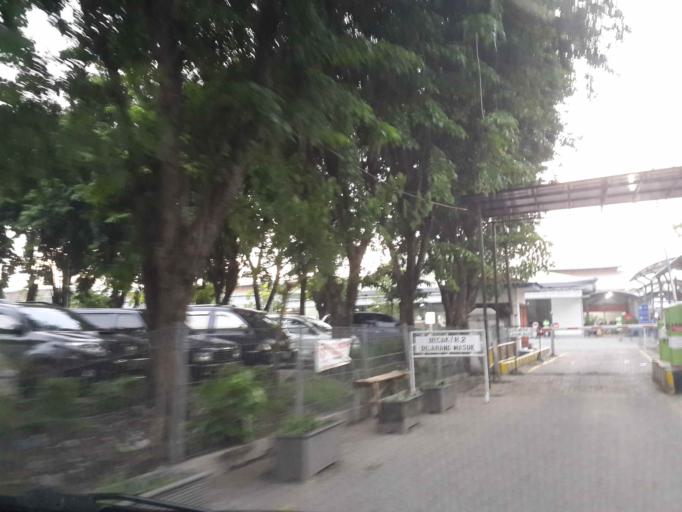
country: ID
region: East Java
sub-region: Kota Surabaya
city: Surabaya
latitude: -7.2486
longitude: 112.7320
